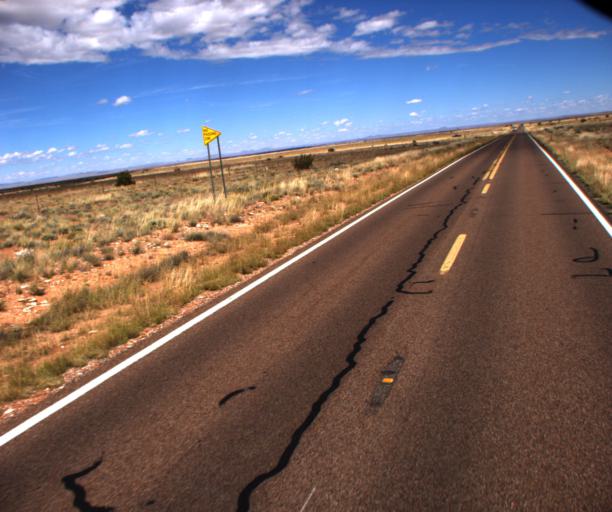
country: US
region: Arizona
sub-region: Navajo County
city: Holbrook
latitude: 34.7336
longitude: -110.2793
